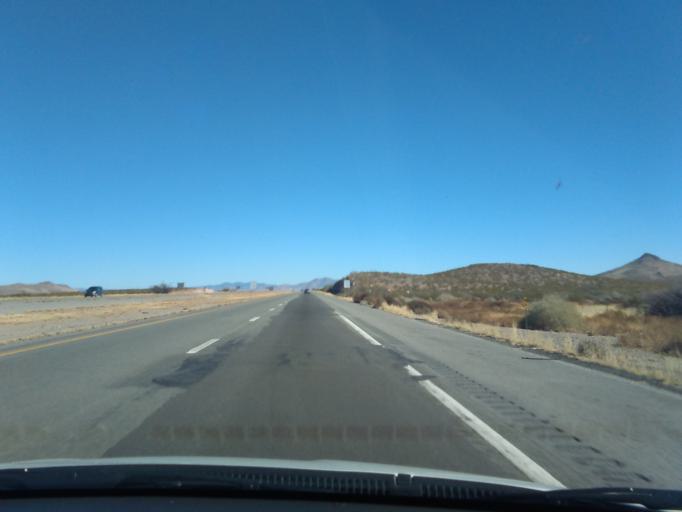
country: US
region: New Mexico
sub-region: Hidalgo County
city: Lordsburg
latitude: 32.3208
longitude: -108.8095
